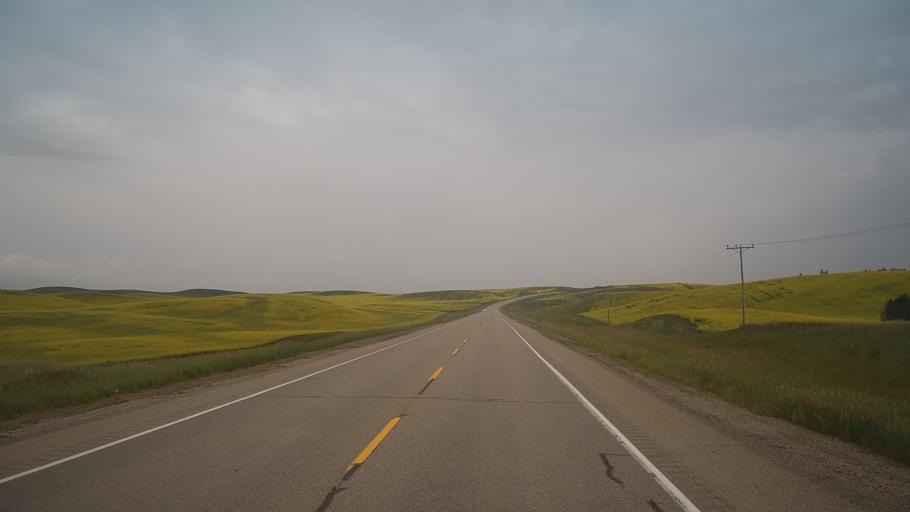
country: CA
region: Saskatchewan
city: Biggar
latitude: 52.0549
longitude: -107.7525
